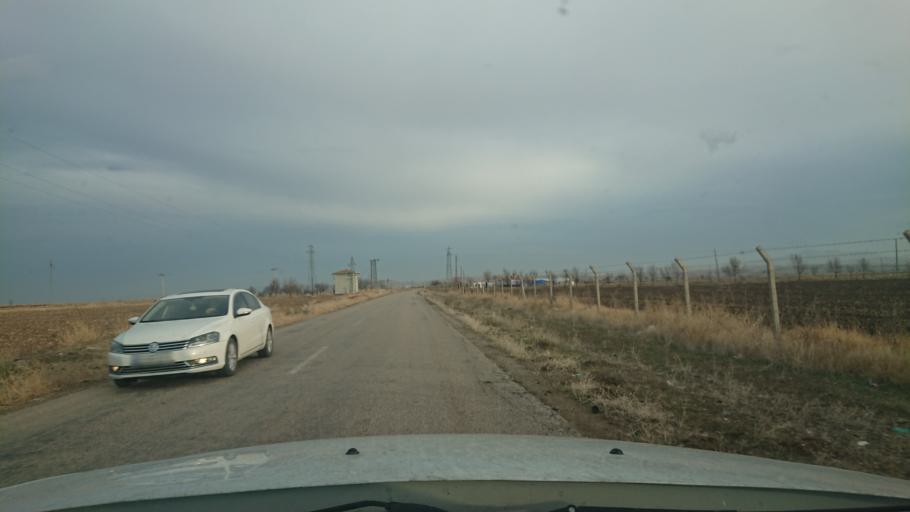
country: TR
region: Aksaray
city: Yesilova
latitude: 38.4262
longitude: 33.8350
